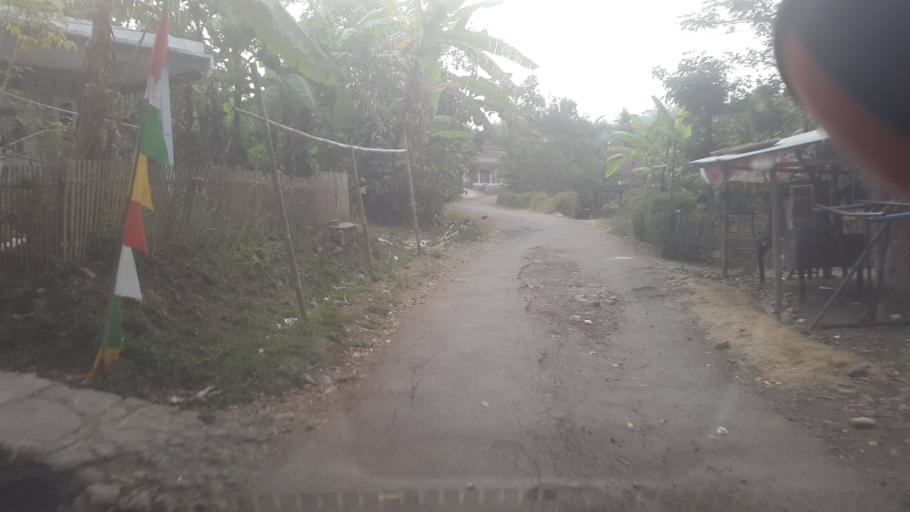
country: ID
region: West Java
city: Sukamaju
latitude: -7.0051
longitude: 106.8867
